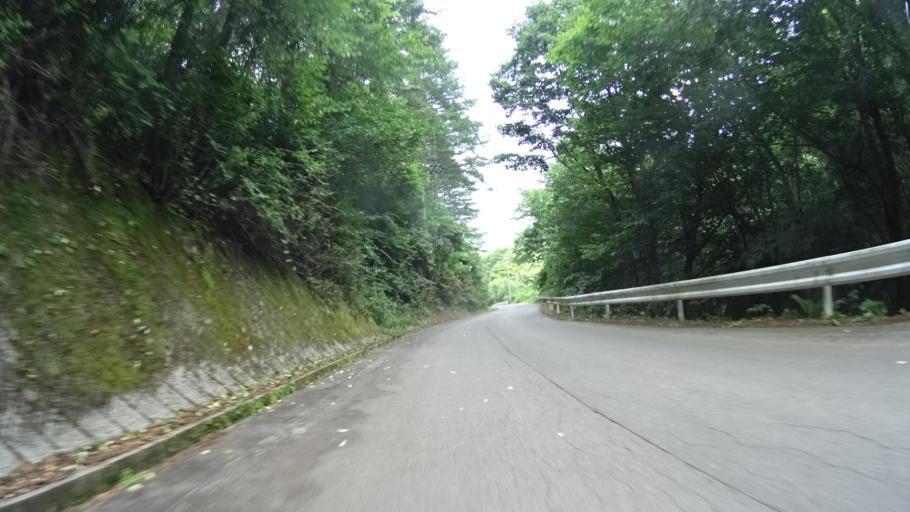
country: JP
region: Nagano
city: Saku
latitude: 36.1191
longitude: 138.6104
